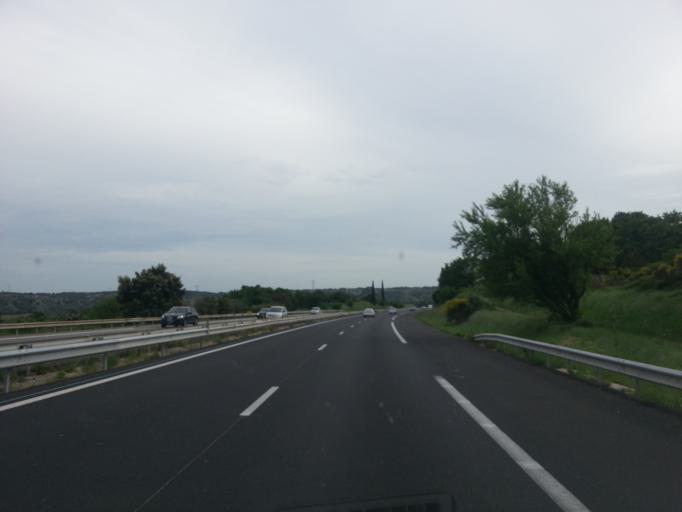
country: FR
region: Languedoc-Roussillon
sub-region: Departement du Gard
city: Roquemaure
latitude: 44.0403
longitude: 4.7651
